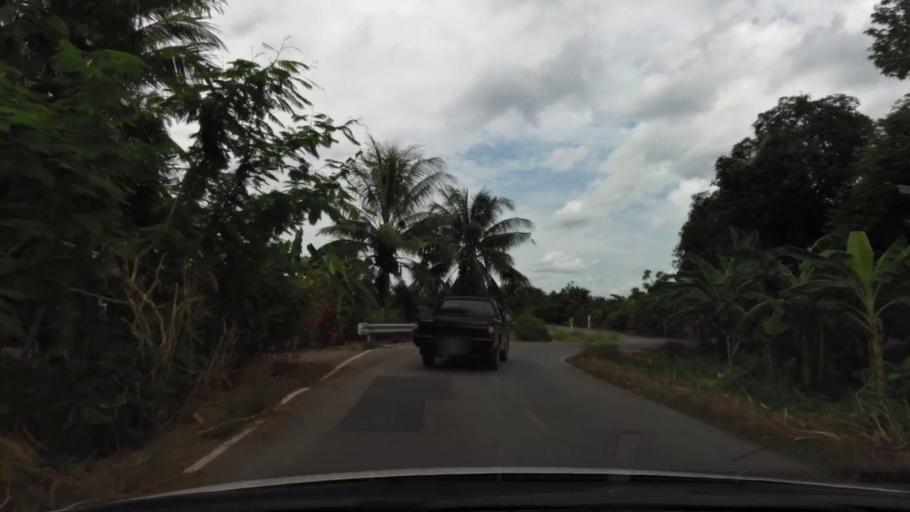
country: TH
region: Samut Sakhon
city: Ban Phaeo
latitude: 13.5612
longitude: 100.0415
